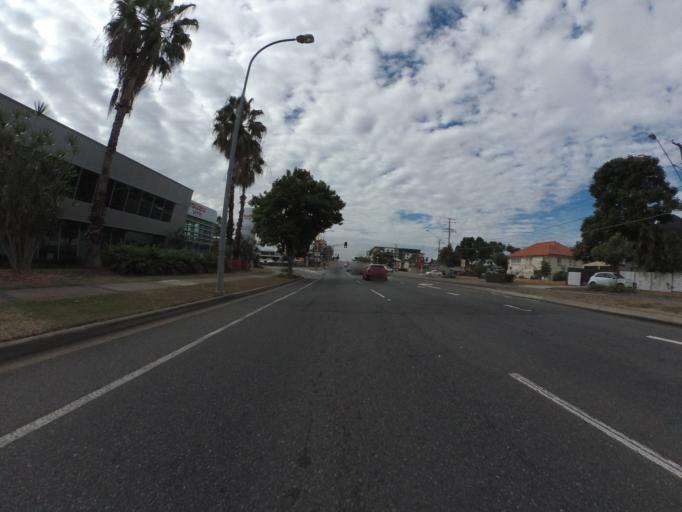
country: AU
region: Queensland
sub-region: Brisbane
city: Cannon Hill
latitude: -27.4688
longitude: 153.0924
